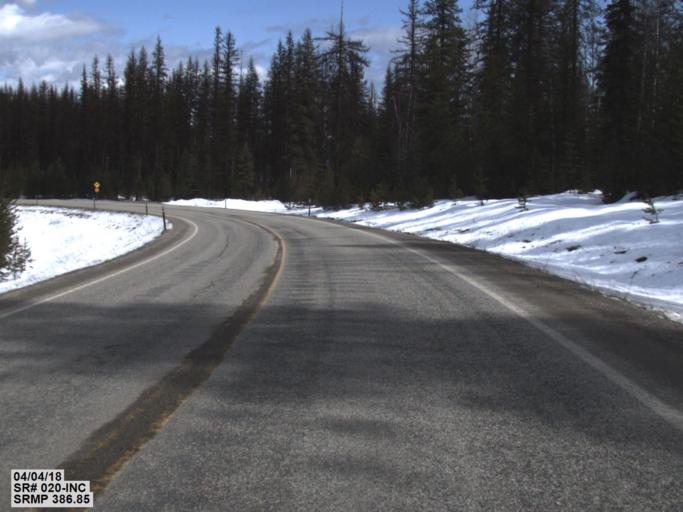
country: CA
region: British Columbia
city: Fruitvale
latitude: 48.6812
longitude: -117.4526
